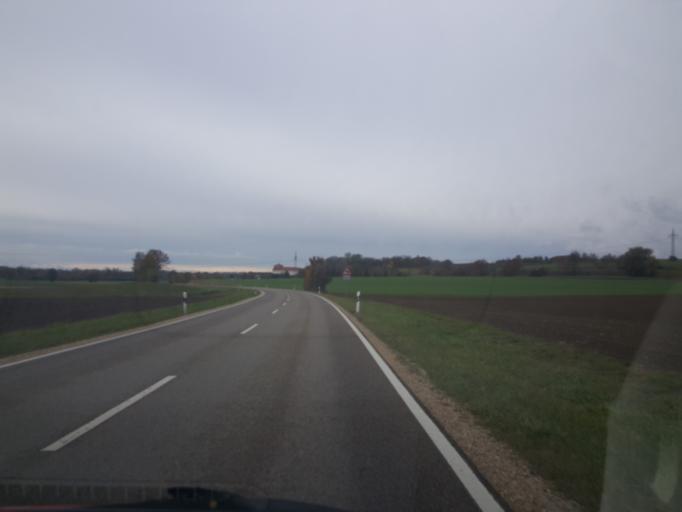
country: DE
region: Bavaria
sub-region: Upper Bavaria
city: Rennertshofen
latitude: 48.7491
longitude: 11.0347
